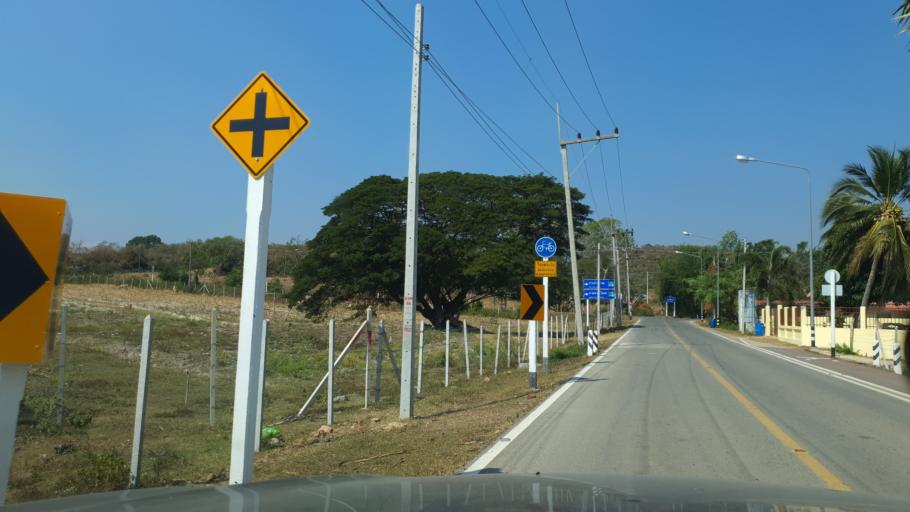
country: TH
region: Prachuap Khiri Khan
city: Sam Roi Yot
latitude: 12.2849
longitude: 99.9717
